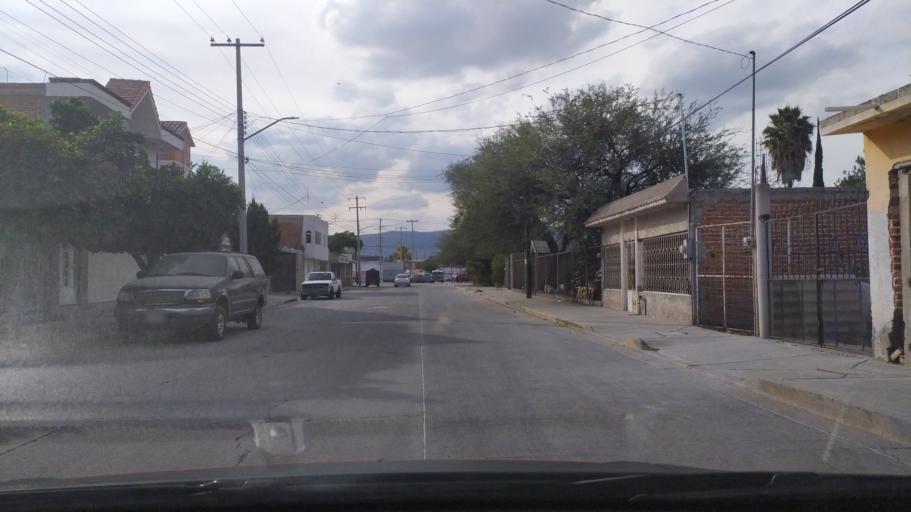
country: MX
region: Guanajuato
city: San Francisco del Rincon
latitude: 21.0054
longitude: -101.8508
